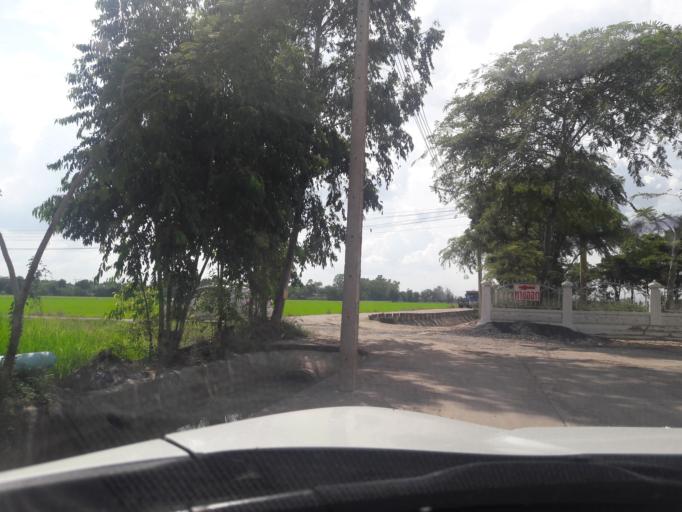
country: TH
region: Lop Buri
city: Ban Mi
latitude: 14.9690
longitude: 100.5238
